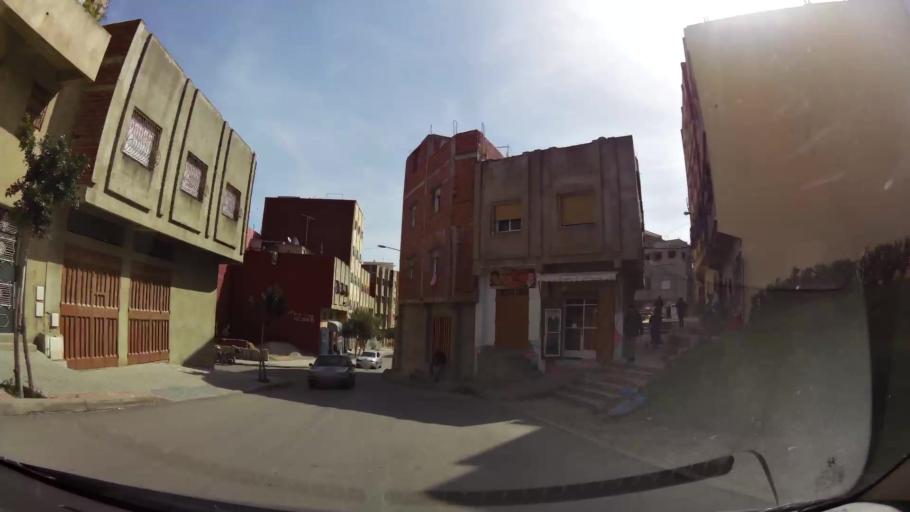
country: MA
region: Tanger-Tetouan
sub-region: Tanger-Assilah
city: Tangier
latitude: 35.7317
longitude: -5.8059
